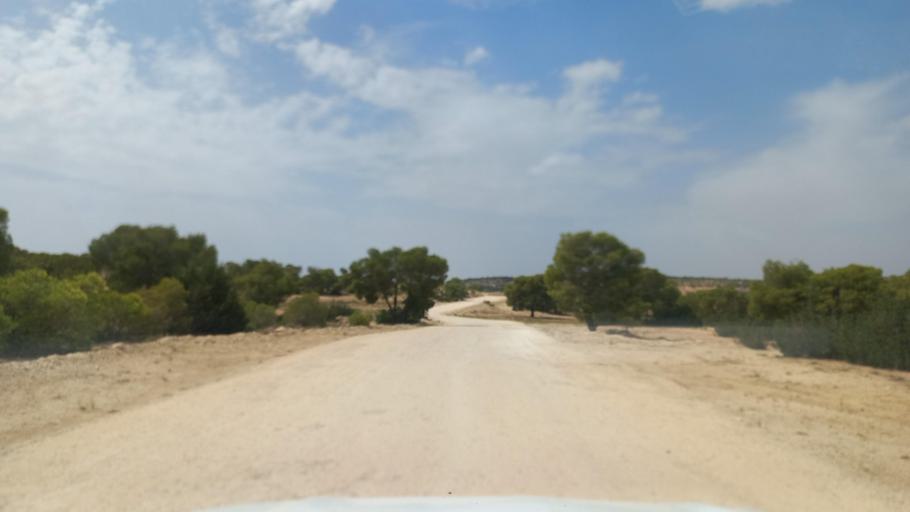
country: TN
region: Al Qasrayn
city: Kasserine
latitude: 35.3838
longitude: 8.8702
